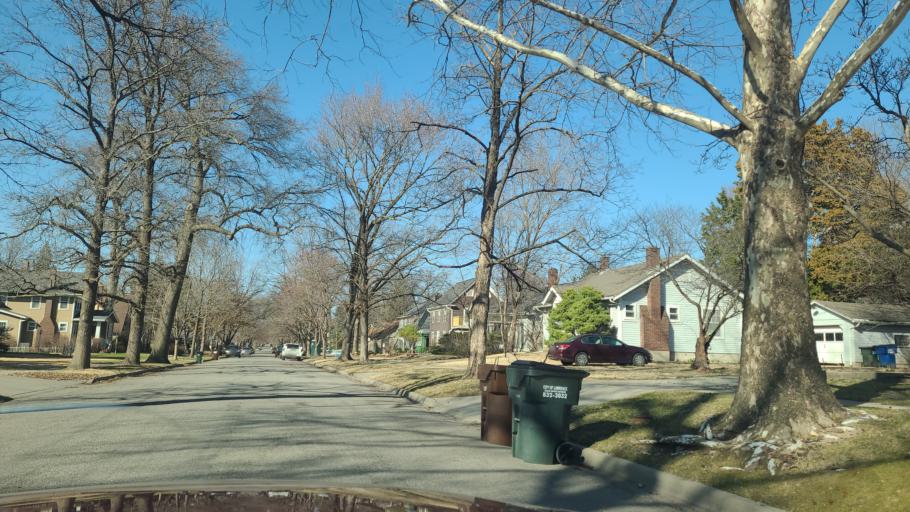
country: US
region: Kansas
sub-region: Douglas County
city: Lawrence
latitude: 38.9433
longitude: -95.2347
